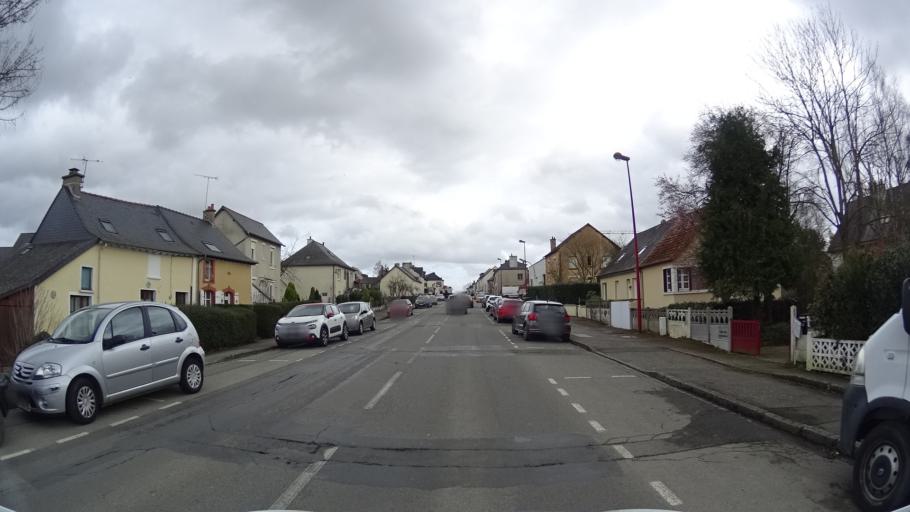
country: FR
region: Brittany
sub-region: Departement d'Ille-et-Vilaine
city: Saint-Gilles
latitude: 48.1562
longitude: -1.8318
